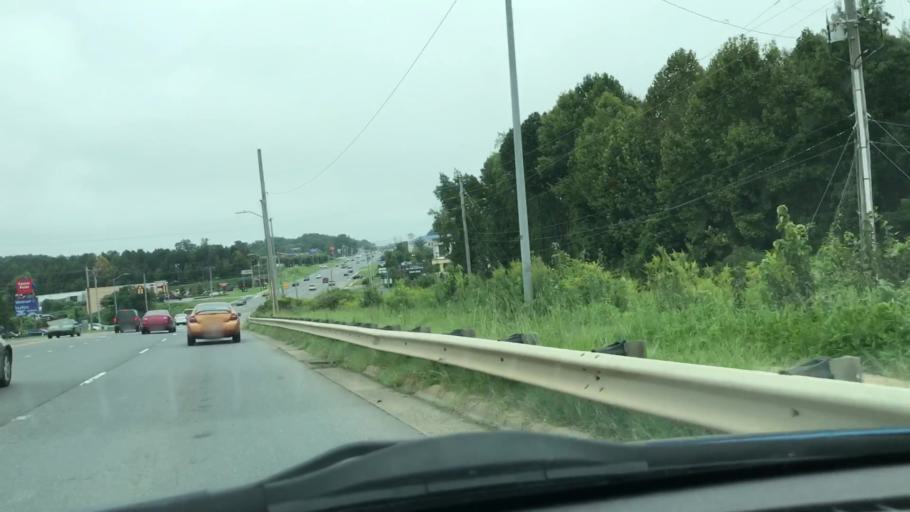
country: US
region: North Carolina
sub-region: Randolph County
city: Asheboro
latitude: 35.6972
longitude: -79.7890
